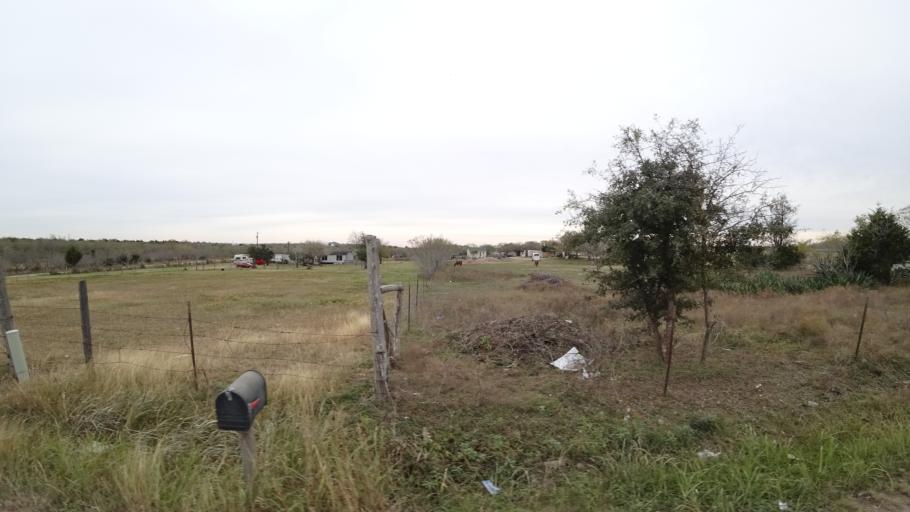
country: US
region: Texas
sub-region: Travis County
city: Garfield
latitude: 30.1074
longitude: -97.5879
